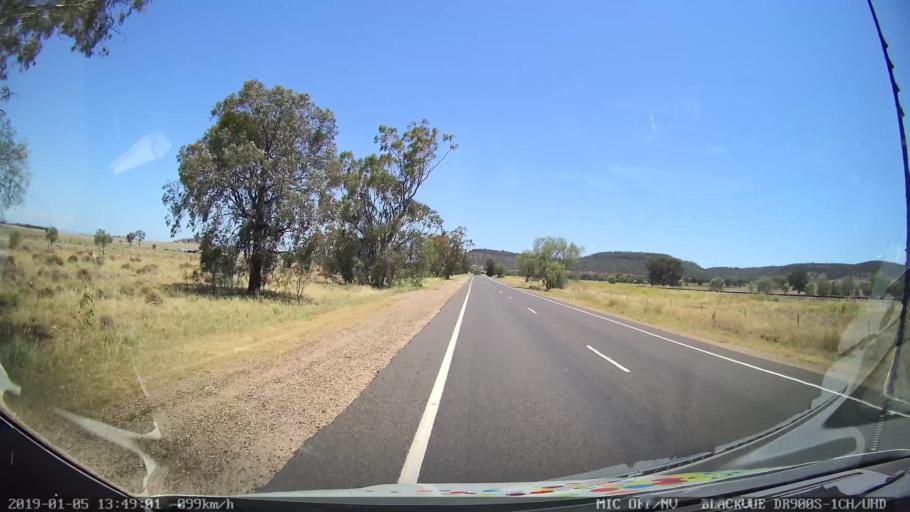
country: AU
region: New South Wales
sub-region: Gunnedah
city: Gunnedah
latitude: -31.0101
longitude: 150.2750
